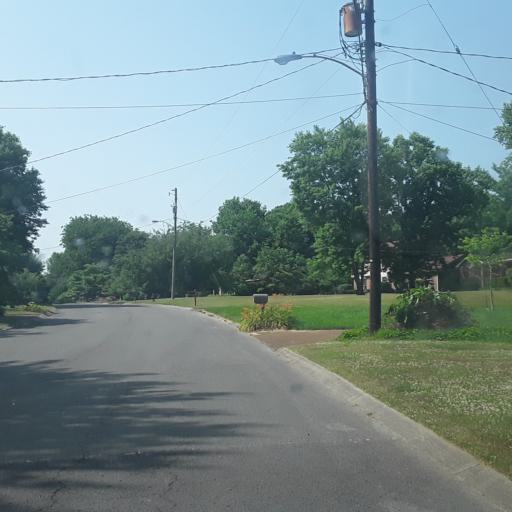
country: US
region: Tennessee
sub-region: Williamson County
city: Brentwood
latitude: 36.0459
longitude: -86.7511
